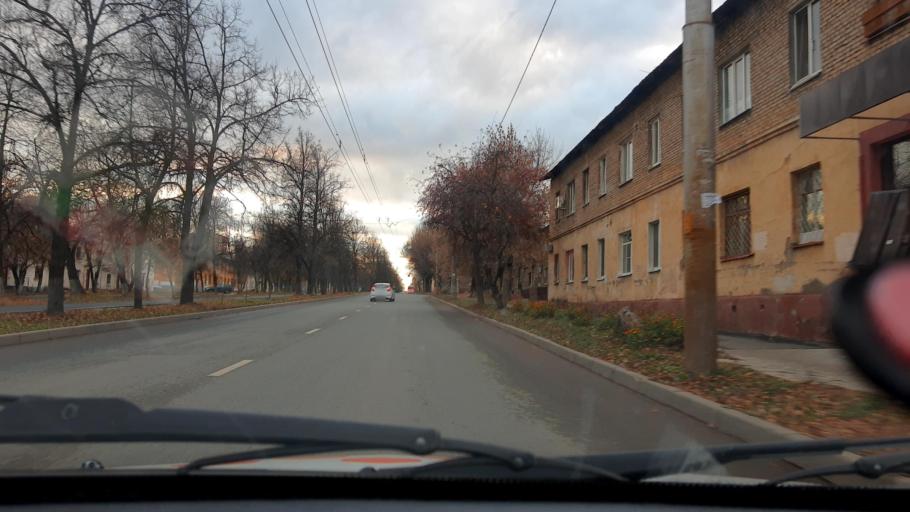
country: RU
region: Bashkortostan
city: Ufa
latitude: 54.8121
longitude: 56.1141
